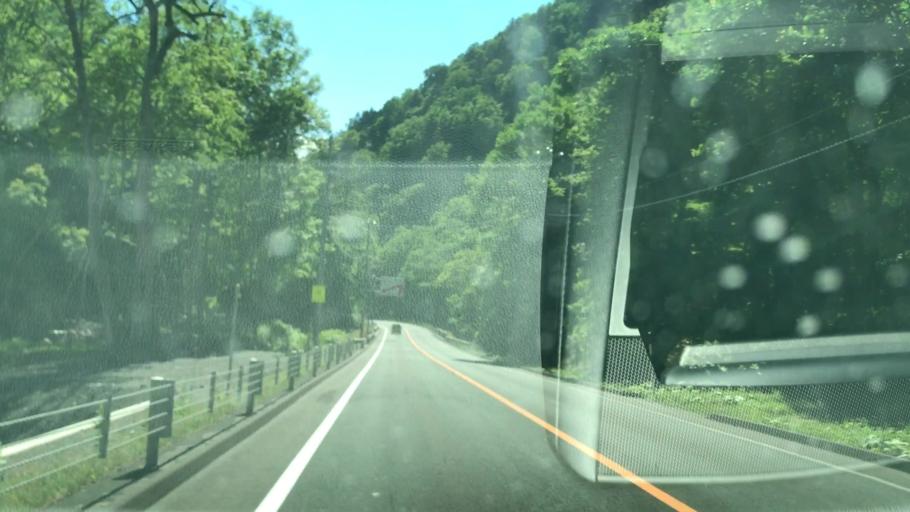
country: JP
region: Hokkaido
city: Shimo-furano
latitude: 42.9662
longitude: 142.6256
